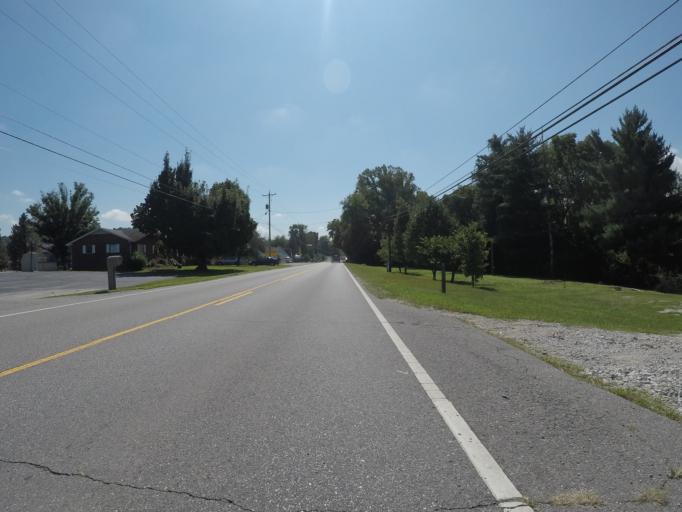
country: US
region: Ohio
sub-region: Lawrence County
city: South Point
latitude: 38.4542
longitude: -82.5955
